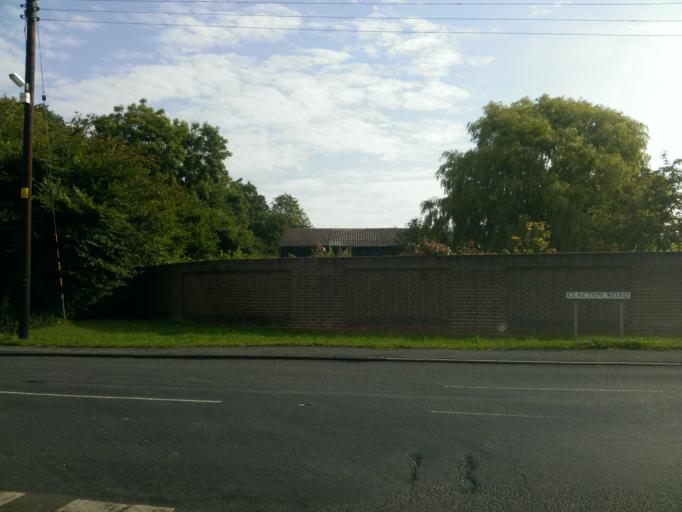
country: GB
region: England
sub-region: Essex
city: Little Clacton
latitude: 51.8465
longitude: 1.1204
